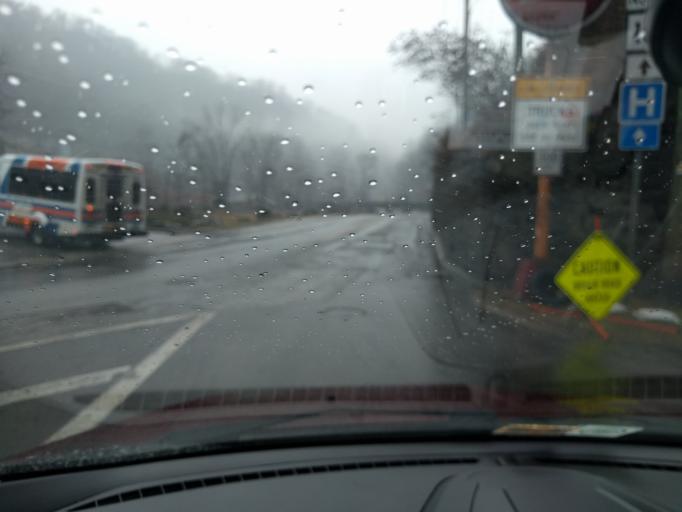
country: US
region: West Virginia
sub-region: McDowell County
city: Welch
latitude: 37.4345
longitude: -81.5855
